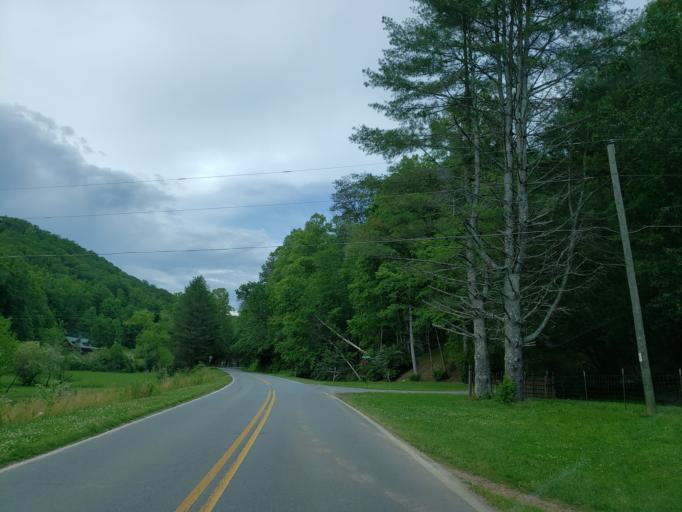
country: US
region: Georgia
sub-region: Fannin County
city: Blue Ridge
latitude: 34.8366
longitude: -84.4015
